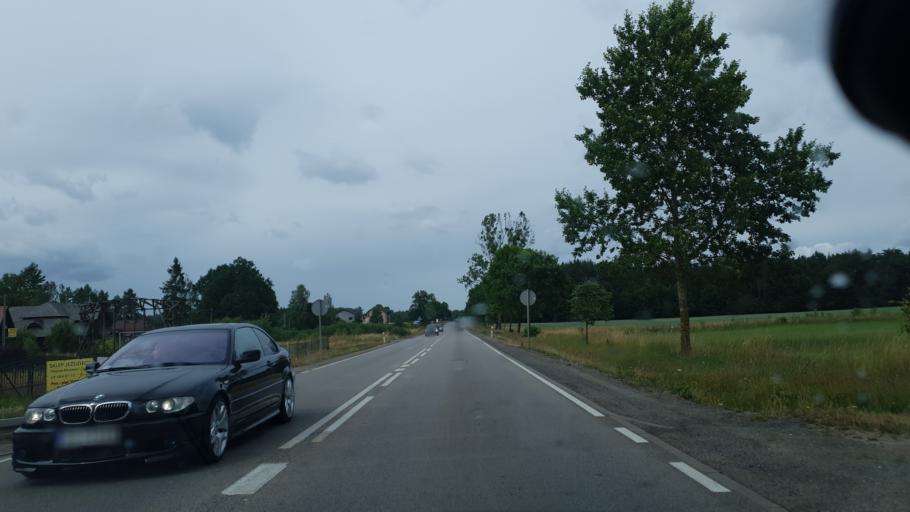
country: PL
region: Pomeranian Voivodeship
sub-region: Powiat kartuski
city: Banino
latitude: 54.3952
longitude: 18.3572
